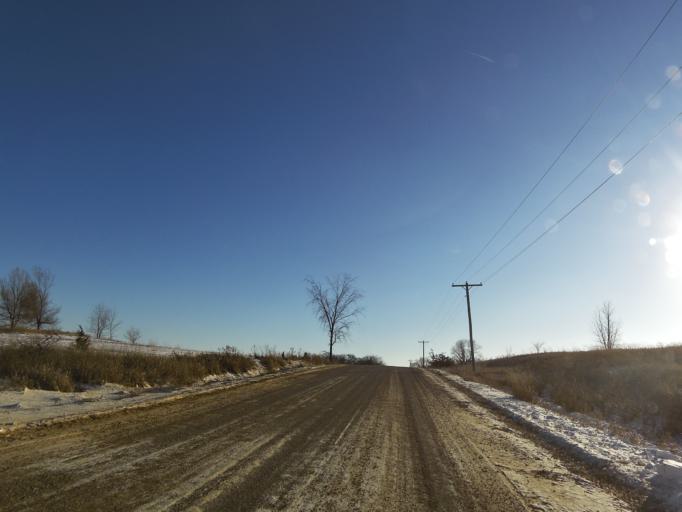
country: US
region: Minnesota
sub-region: Le Sueur County
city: New Prague
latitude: 44.5488
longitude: -93.5529
